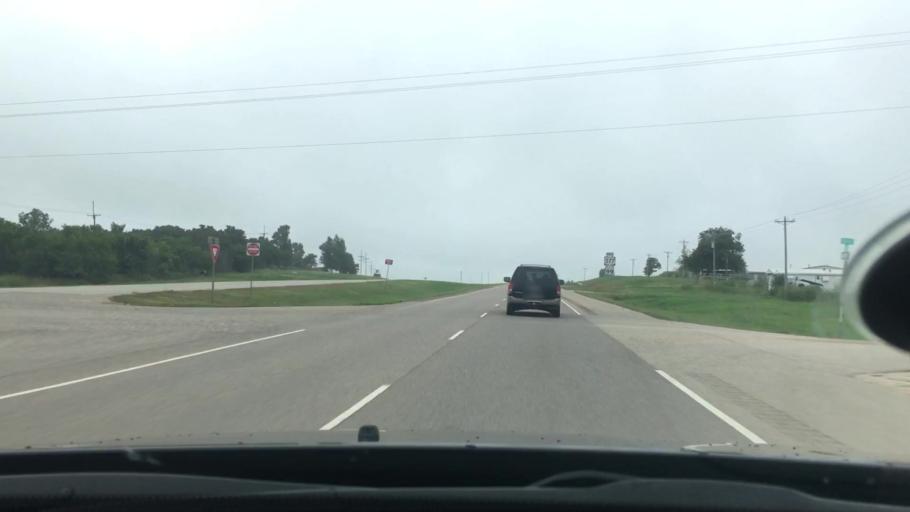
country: US
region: Oklahoma
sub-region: Seminole County
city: Seminole
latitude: 35.3043
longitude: -96.6707
